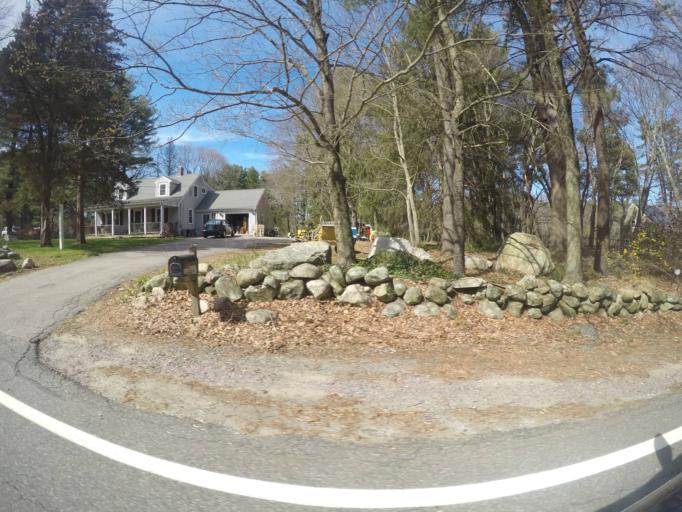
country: US
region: Massachusetts
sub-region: Plymouth County
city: West Bridgewater
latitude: 42.0246
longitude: -71.0622
